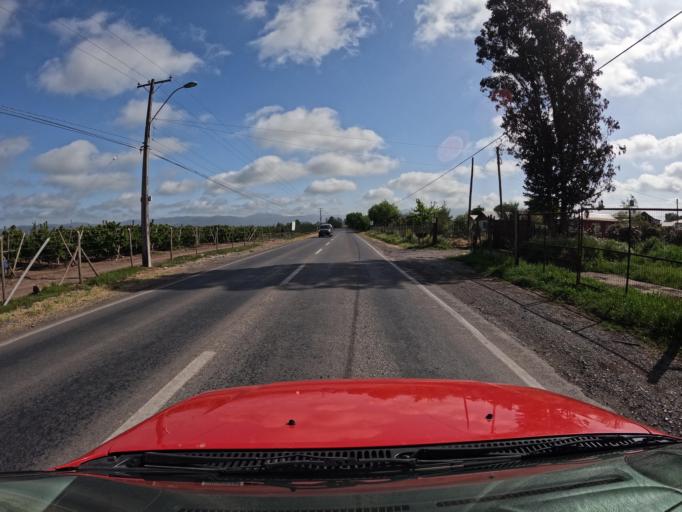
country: CL
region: Maule
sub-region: Provincia de Curico
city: Rauco
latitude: -34.8966
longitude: -71.2736
